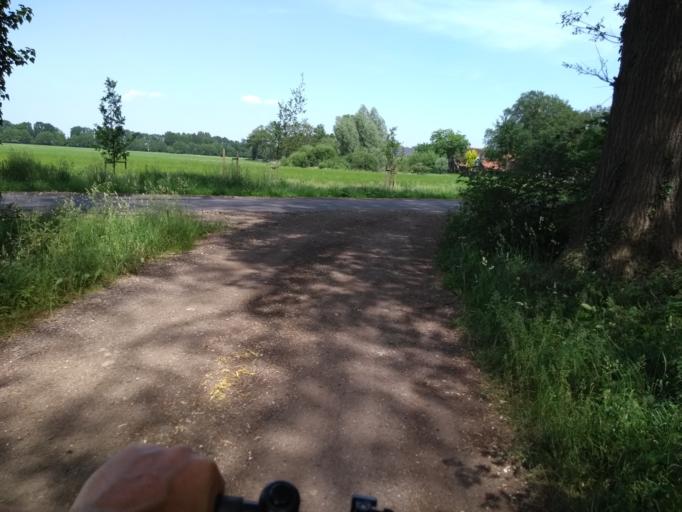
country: NL
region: Overijssel
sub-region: Gemeente Almelo
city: Almelo
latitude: 52.3628
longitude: 6.6992
